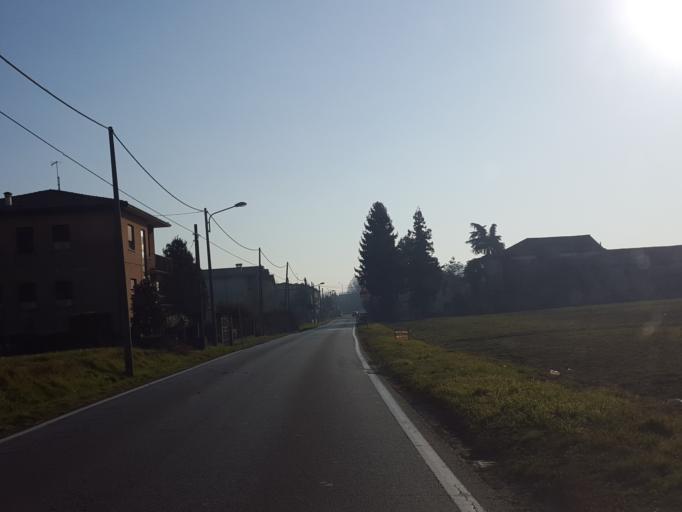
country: IT
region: Veneto
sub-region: Provincia di Vicenza
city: Lisiera
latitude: 45.5731
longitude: 11.5938
